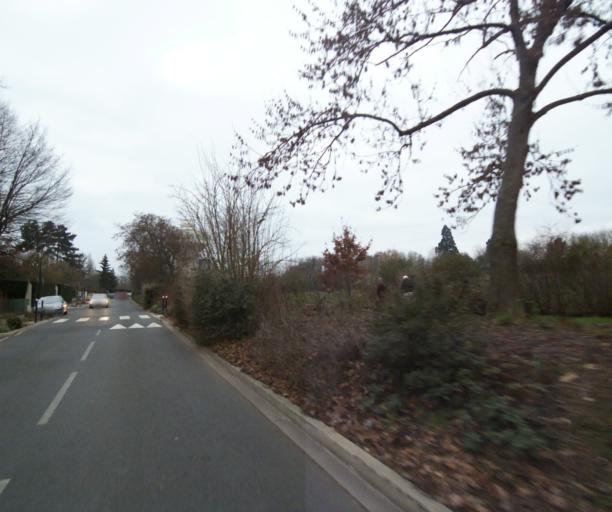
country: FR
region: Ile-de-France
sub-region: Departement des Hauts-de-Seine
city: Vaucresson
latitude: 48.8439
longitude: 2.1676
